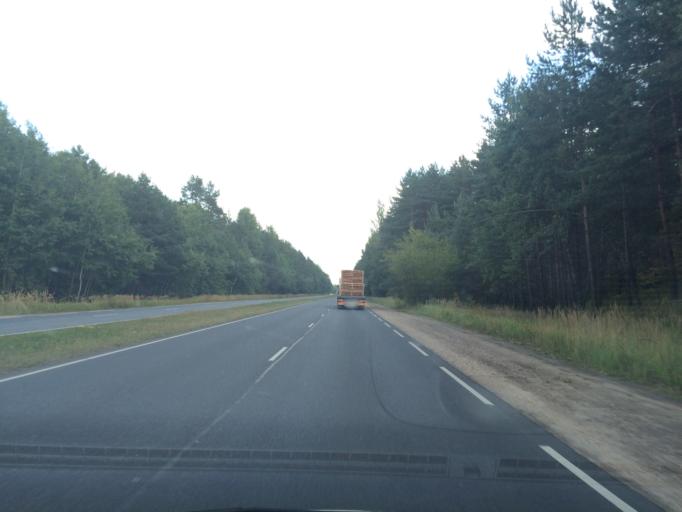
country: LV
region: Kekava
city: Kekava
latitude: 56.8637
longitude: 24.2923
